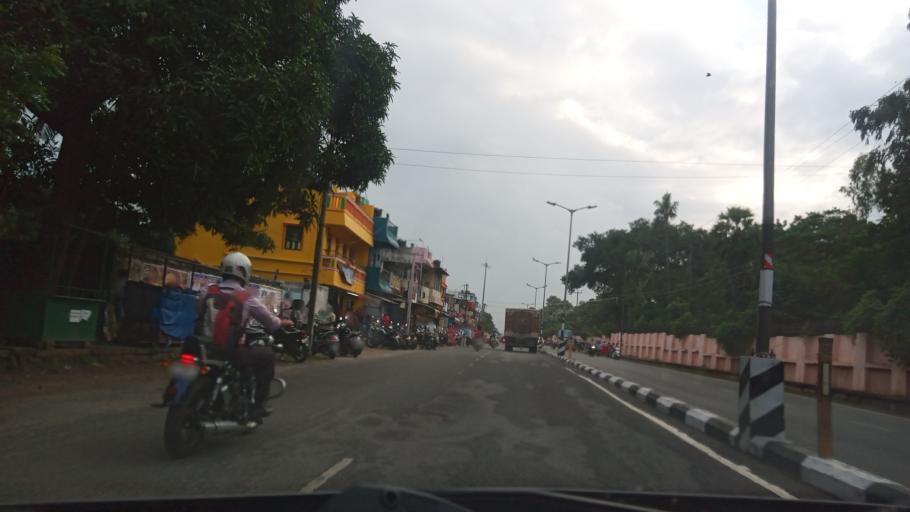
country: IN
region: Tamil Nadu
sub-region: Villupuram
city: Auroville
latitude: 12.0169
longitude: 79.8590
